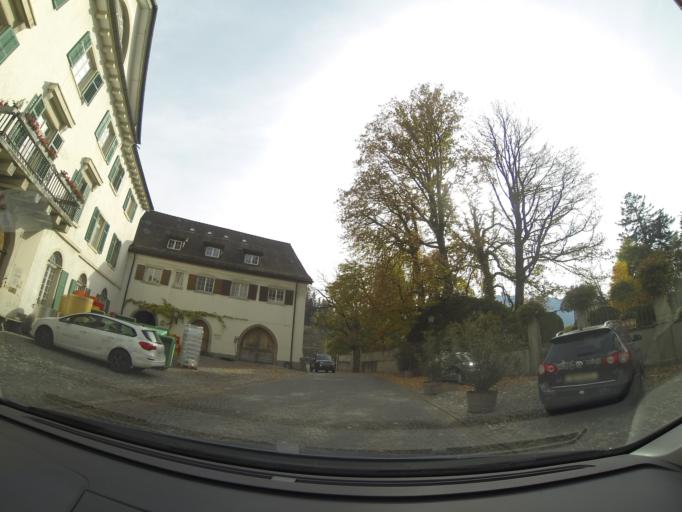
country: CH
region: Grisons
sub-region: Imboden District
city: Tamins
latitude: 46.8245
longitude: 9.4094
